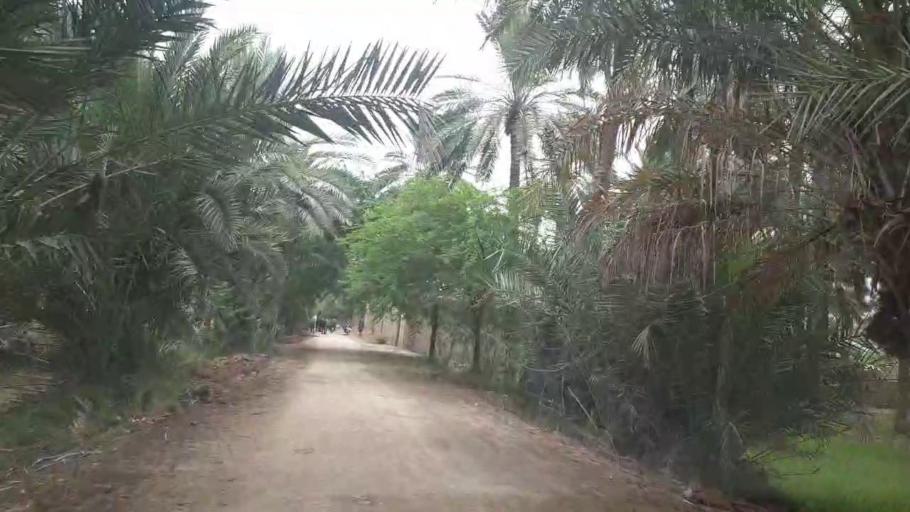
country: PK
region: Sindh
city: Khairpur
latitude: 27.5503
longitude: 68.7444
